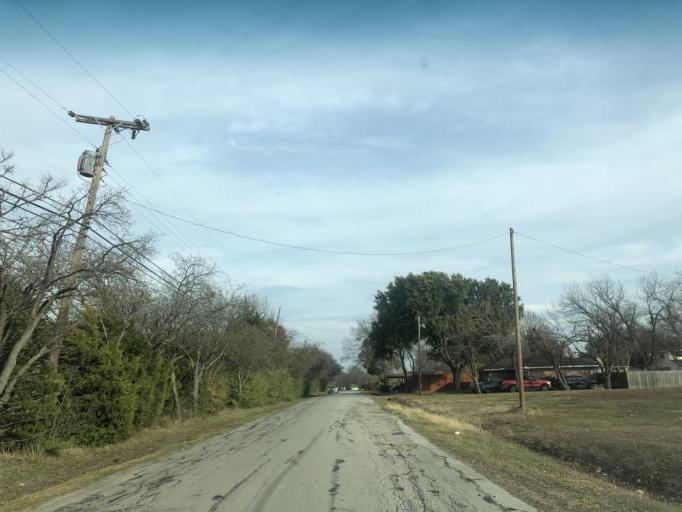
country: US
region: Texas
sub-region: Dallas County
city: Duncanville
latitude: 32.6692
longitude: -96.9043
